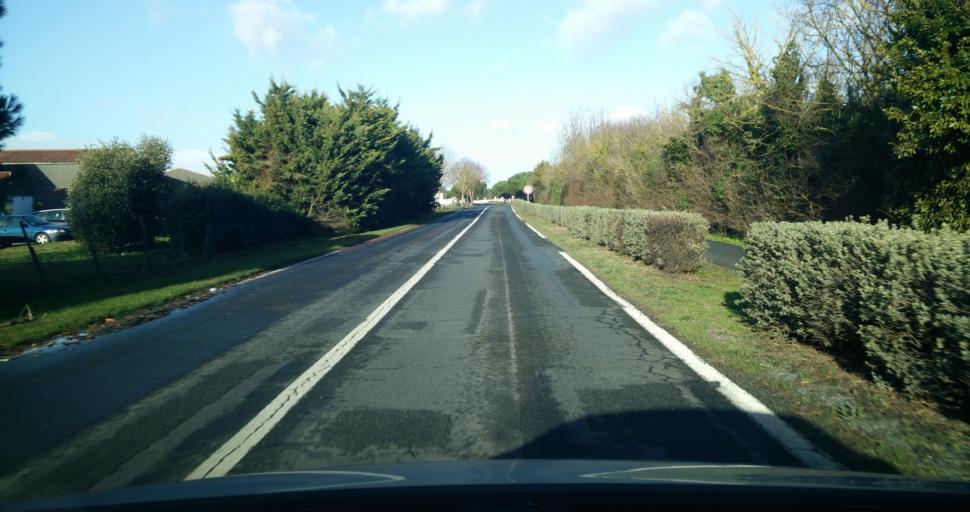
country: FR
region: Poitou-Charentes
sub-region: Departement de la Charente-Maritime
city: Saint-Martin-de-Re
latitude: 46.1963
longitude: -1.3507
